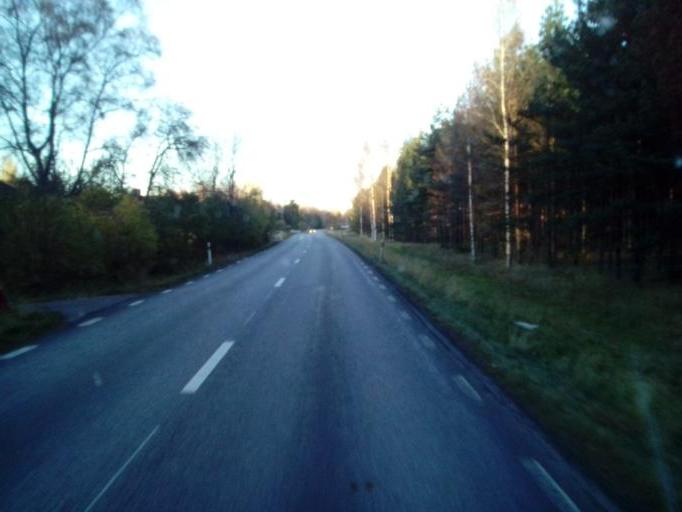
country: SE
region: OErebro
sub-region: Hallsbergs Kommun
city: Palsboda
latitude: 59.0895
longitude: 15.3236
